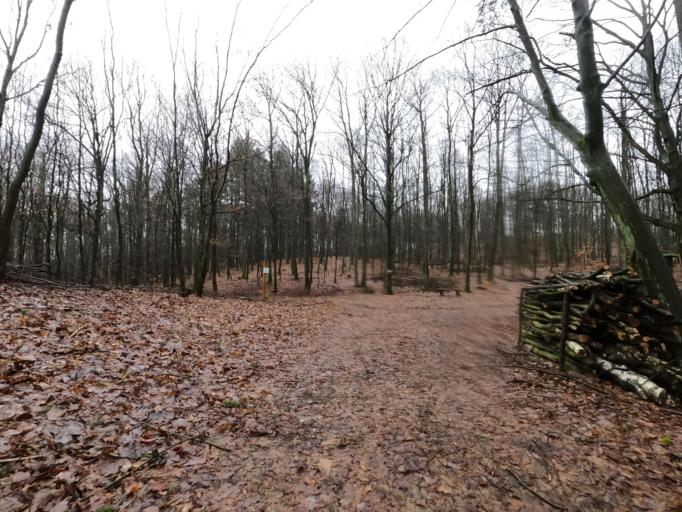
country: PL
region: Greater Poland Voivodeship
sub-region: Powiat pilski
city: Wyrzysk
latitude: 53.1278
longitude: 17.2620
